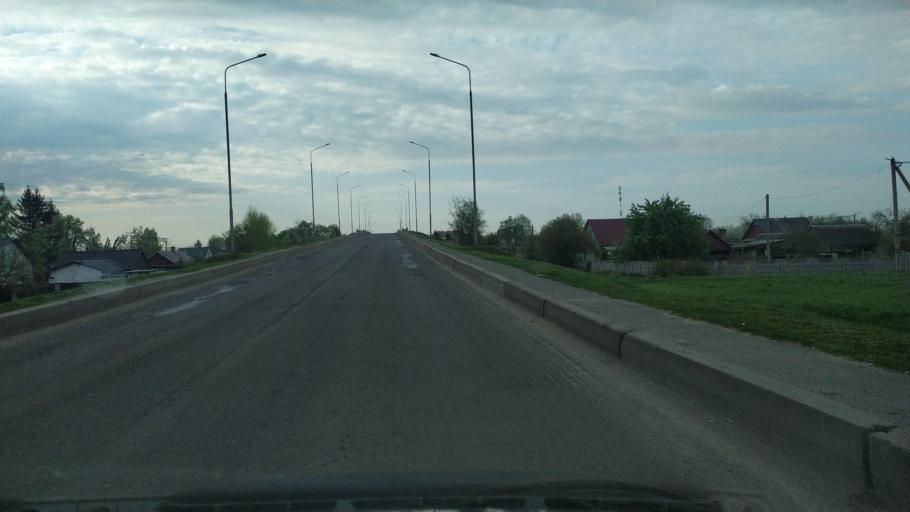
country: BY
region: Brest
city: Zhabinka
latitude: 52.1999
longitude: 24.0080
